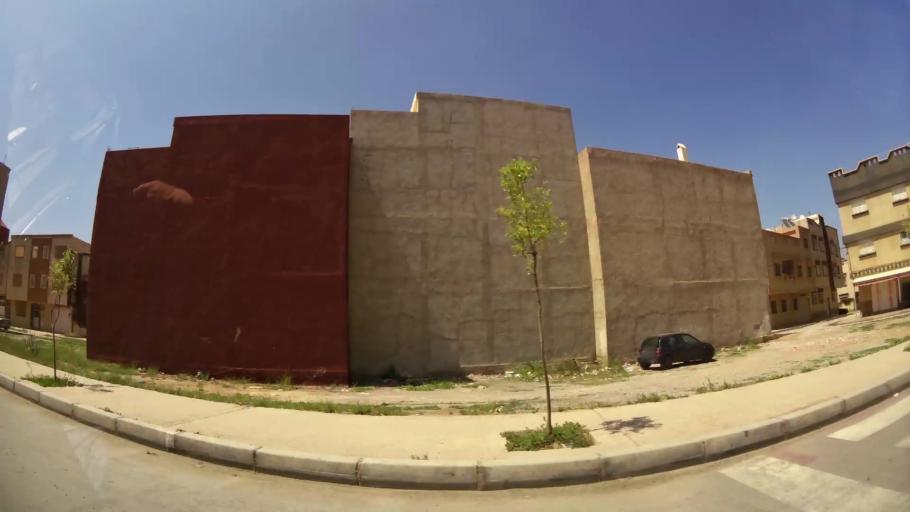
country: MA
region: Oriental
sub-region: Oujda-Angad
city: Oujda
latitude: 34.6928
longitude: -1.8860
